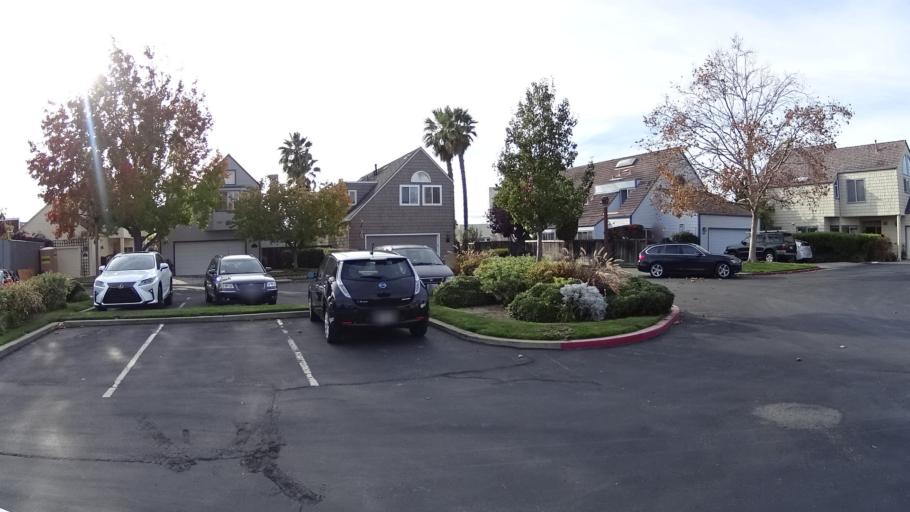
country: US
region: California
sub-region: San Mateo County
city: Foster City
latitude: 37.5443
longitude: -122.2687
